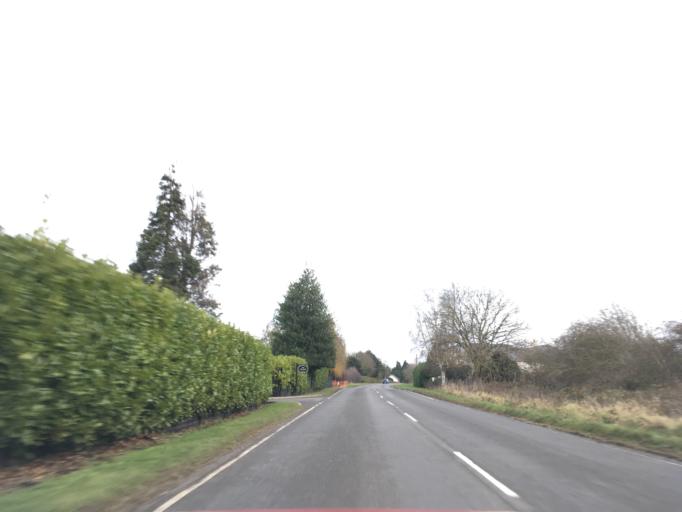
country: GB
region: England
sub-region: Nottinghamshire
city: Ruddington
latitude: 52.8923
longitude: -1.1296
